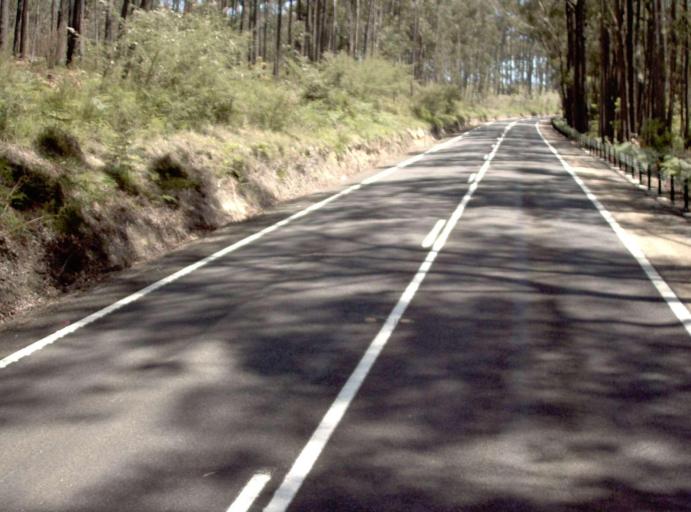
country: AU
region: New South Wales
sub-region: Bombala
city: Bombala
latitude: -37.6559
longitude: 148.8124
